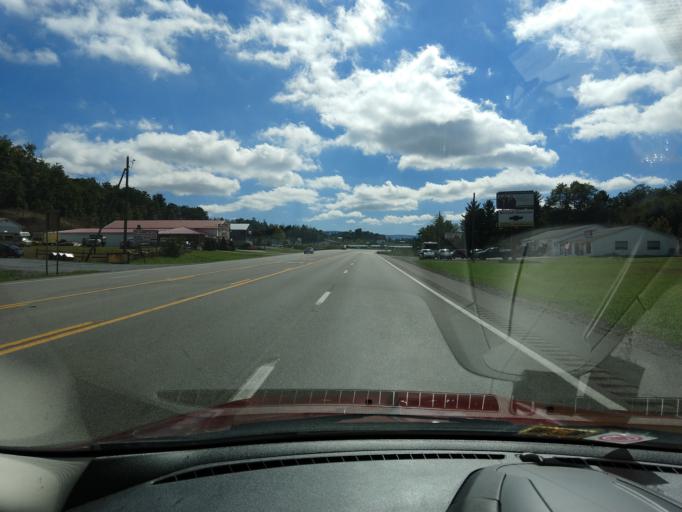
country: US
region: West Virginia
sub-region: Randolph County
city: Elkins
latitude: 38.8786
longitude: -79.8423
